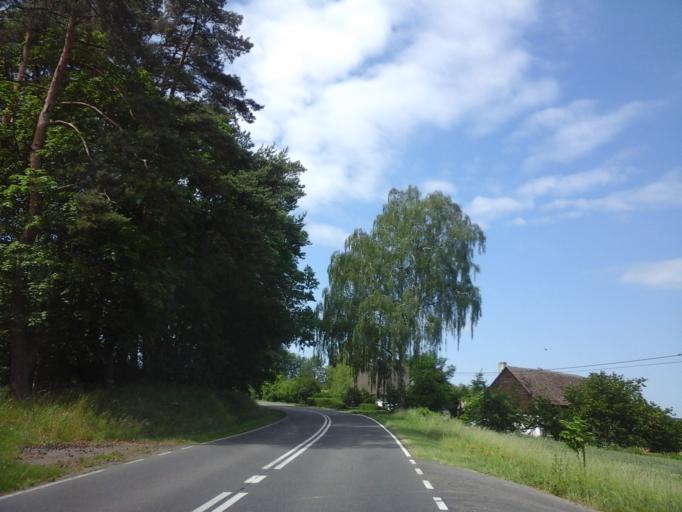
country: PL
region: West Pomeranian Voivodeship
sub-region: Powiat stargardzki
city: Suchan
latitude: 53.2415
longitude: 15.3137
